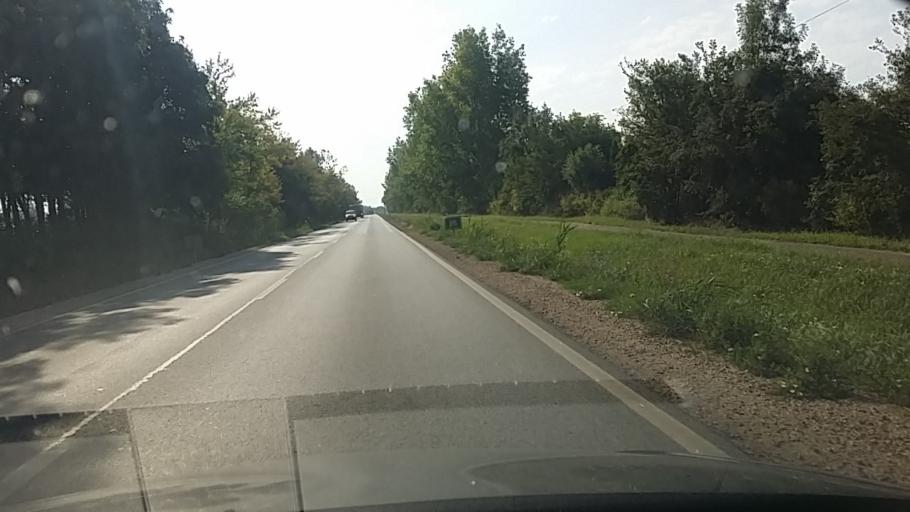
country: HU
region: Bekes
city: Szarvas
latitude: 46.8209
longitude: 20.6685
